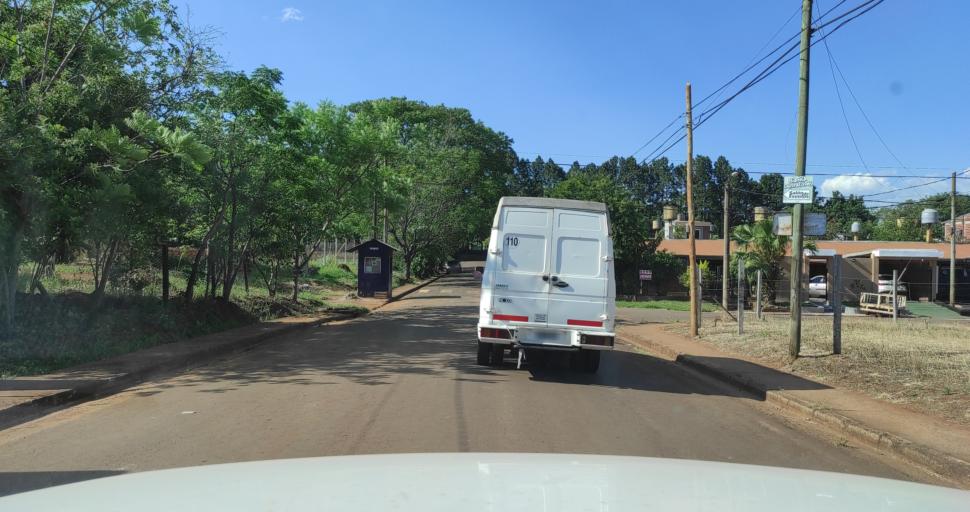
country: AR
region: Misiones
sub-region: Departamento de Capital
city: Posadas
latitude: -27.4125
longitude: -55.9223
